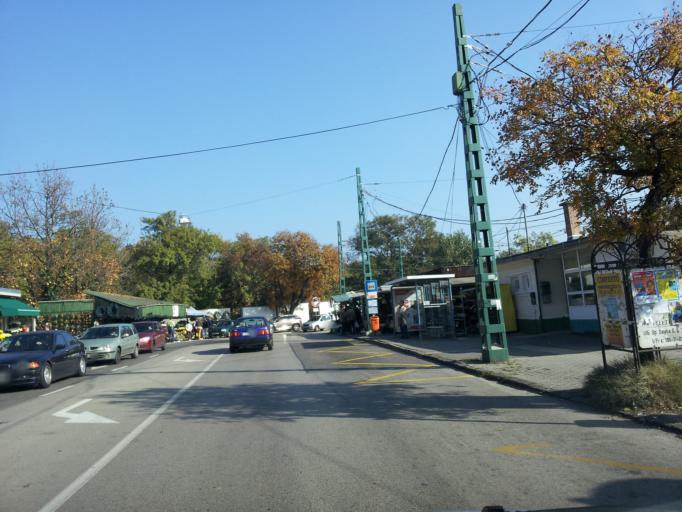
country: HU
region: Budapest
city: Budapest XII. keruelet
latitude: 47.4819
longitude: 18.9990
